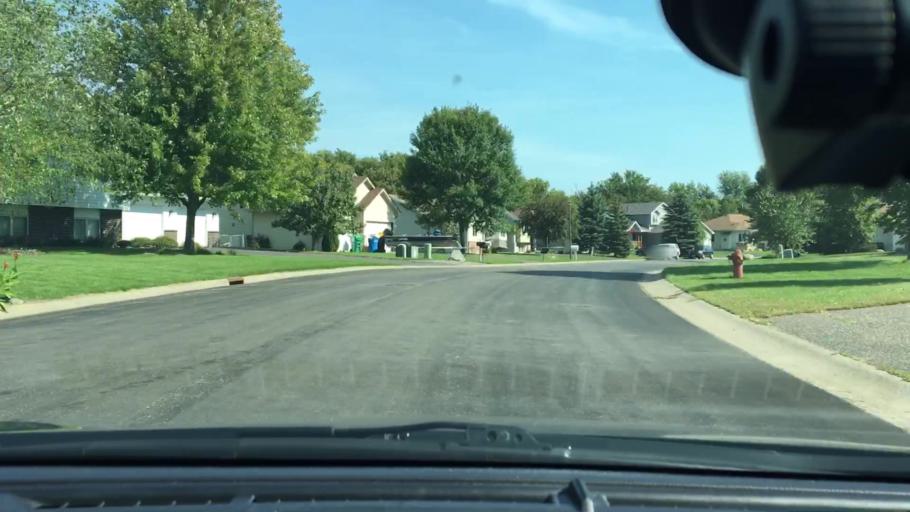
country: US
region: Minnesota
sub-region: Wright County
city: Saint Michael
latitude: 45.2046
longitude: -93.6779
